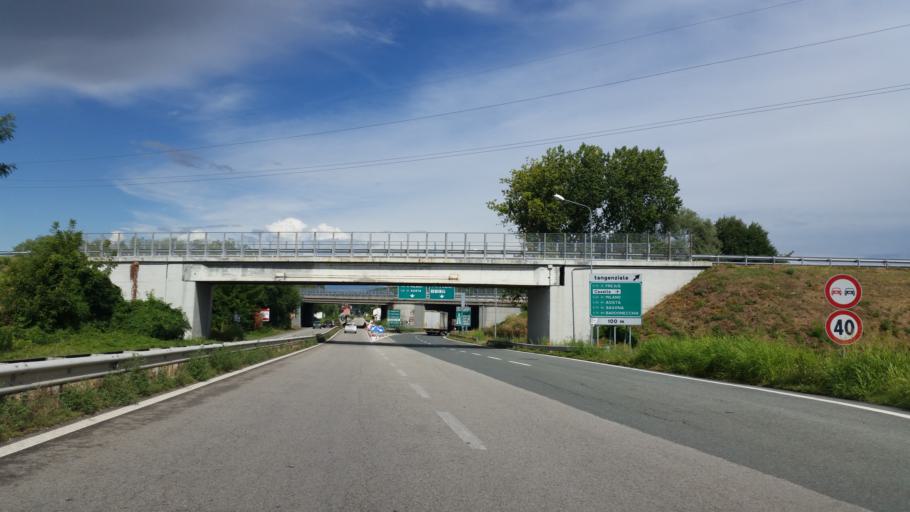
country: IT
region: Piedmont
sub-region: Provincia di Torino
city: Cambiano
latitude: 44.9586
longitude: 7.7844
